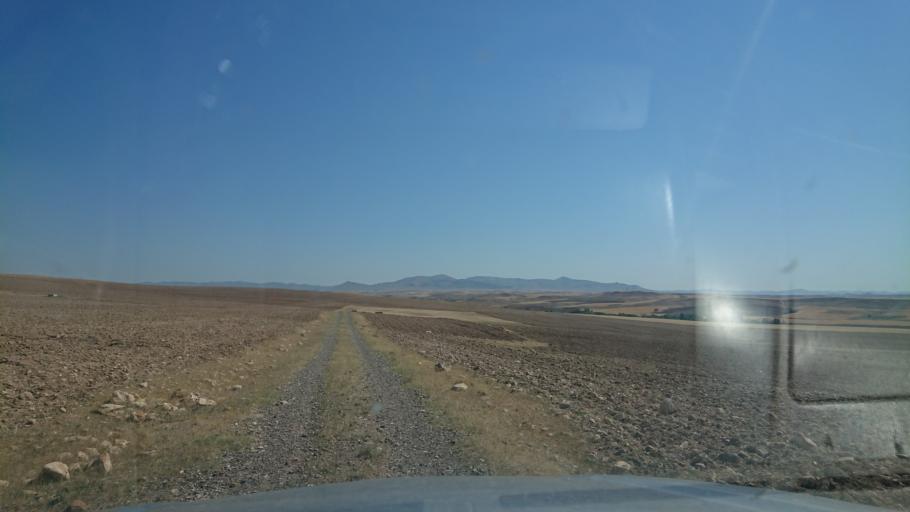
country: TR
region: Aksaray
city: Sariyahsi
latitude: 39.0522
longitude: 33.8887
